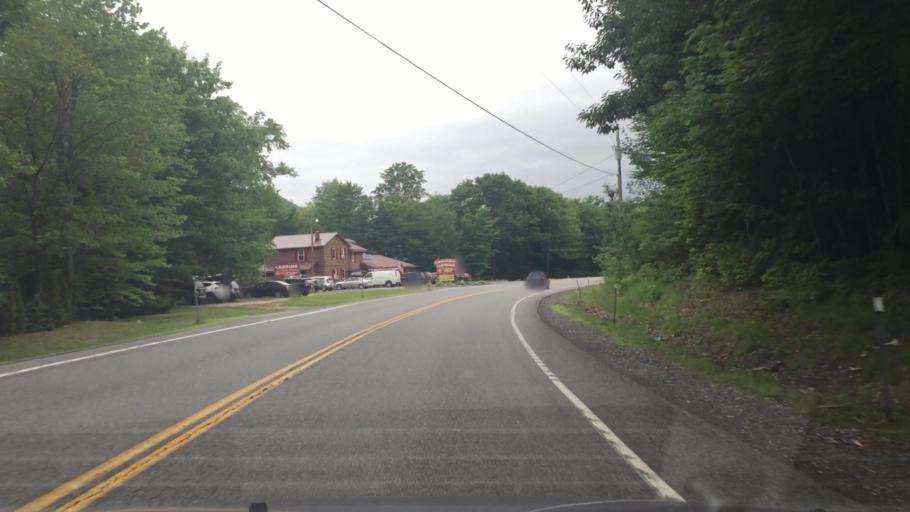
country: US
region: New Hampshire
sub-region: Carroll County
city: North Conway
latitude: 44.1351
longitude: -71.3600
